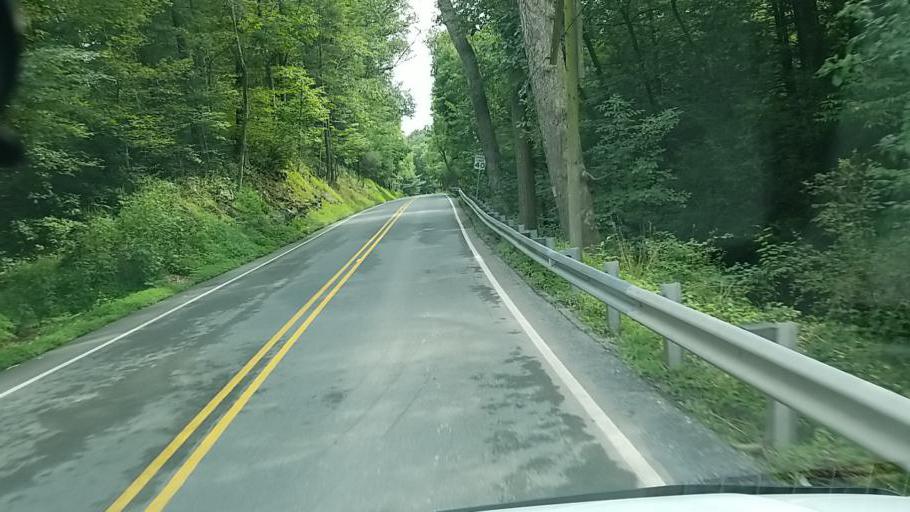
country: US
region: Pennsylvania
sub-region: Dauphin County
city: Elizabethville
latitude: 40.6235
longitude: -76.7857
